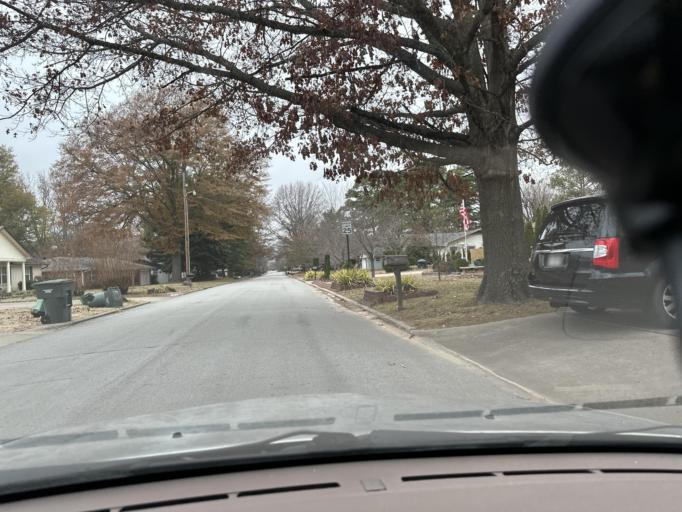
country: US
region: Arkansas
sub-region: Washington County
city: Johnson
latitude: 36.1096
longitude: -94.1381
